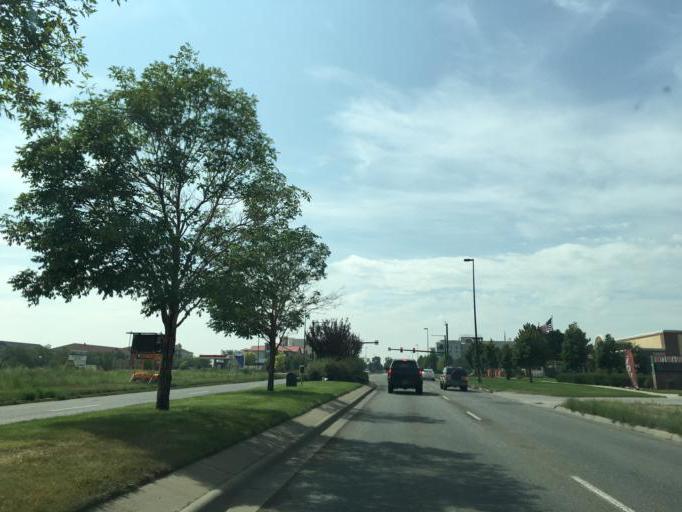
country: US
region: Colorado
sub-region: Adams County
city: Aurora
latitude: 39.8270
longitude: -104.7719
